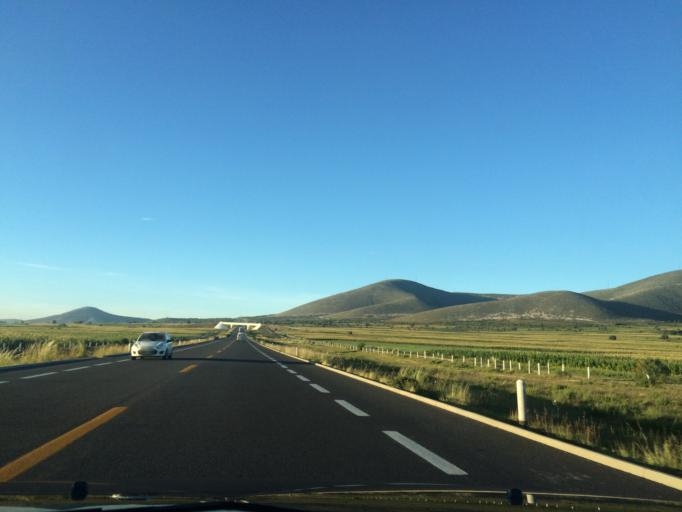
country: MX
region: Puebla
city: Morelos Canada
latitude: 18.7473
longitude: -97.4792
